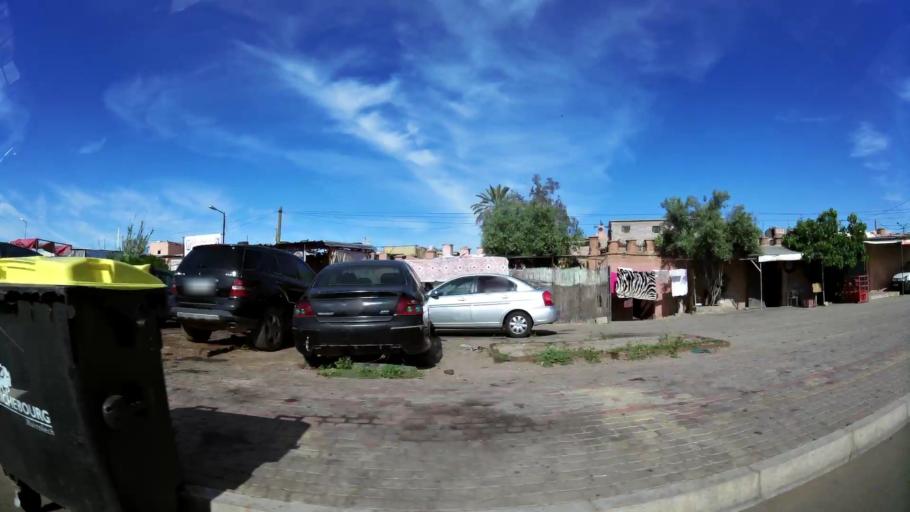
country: MA
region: Marrakech-Tensift-Al Haouz
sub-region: Marrakech
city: Marrakesh
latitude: 31.6440
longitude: -8.0397
